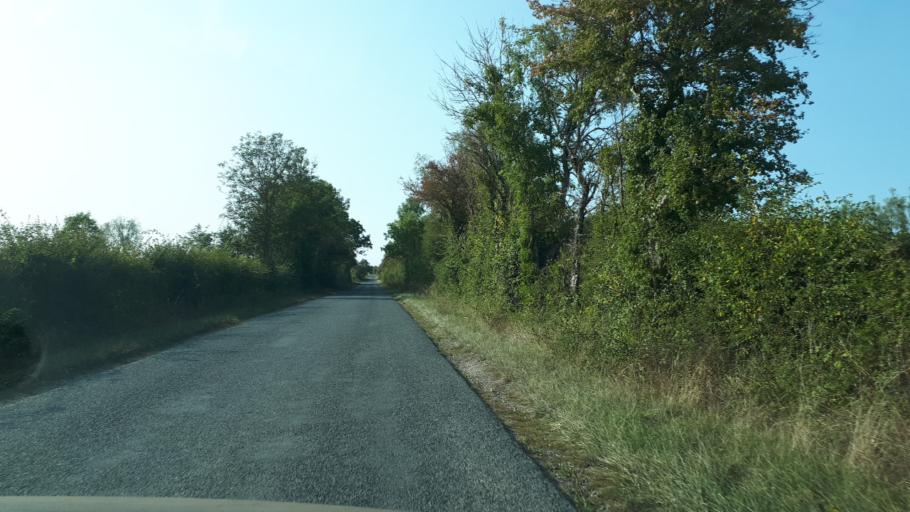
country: FR
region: Centre
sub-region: Departement du Cher
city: Menetou-Salon
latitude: 47.2232
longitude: 2.5293
